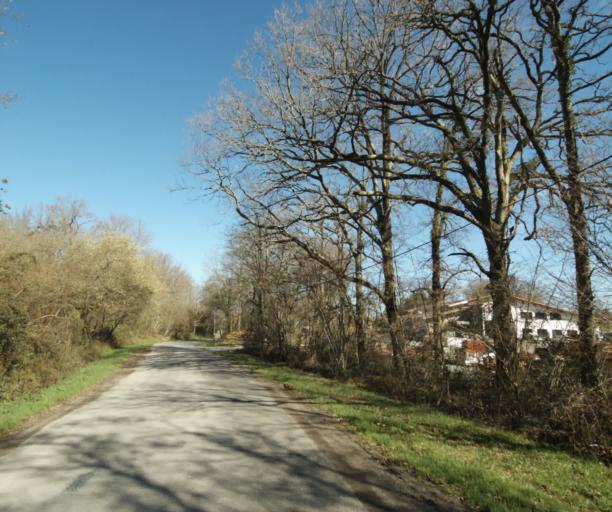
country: FR
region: Aquitaine
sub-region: Departement des Pyrenees-Atlantiques
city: Urrugne
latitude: 43.3638
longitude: -1.6843
